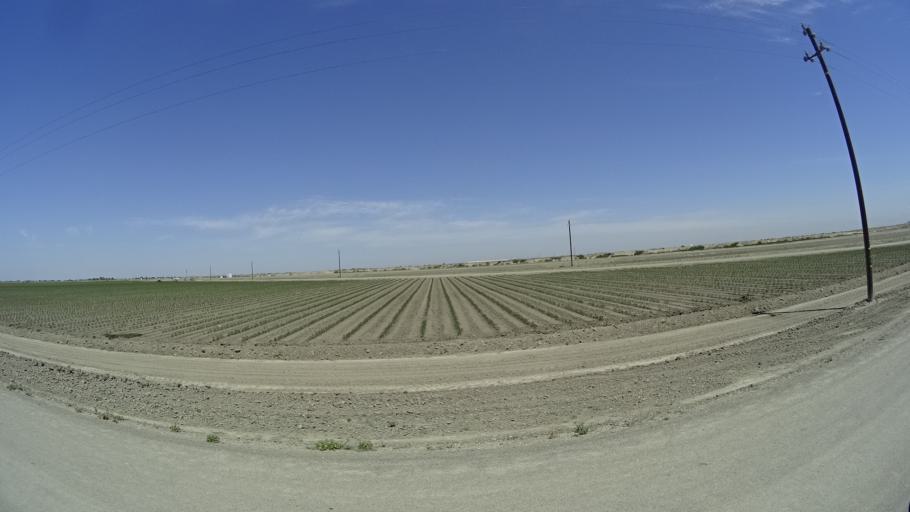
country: US
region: California
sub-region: Kings County
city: Stratford
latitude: 36.1233
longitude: -119.7006
